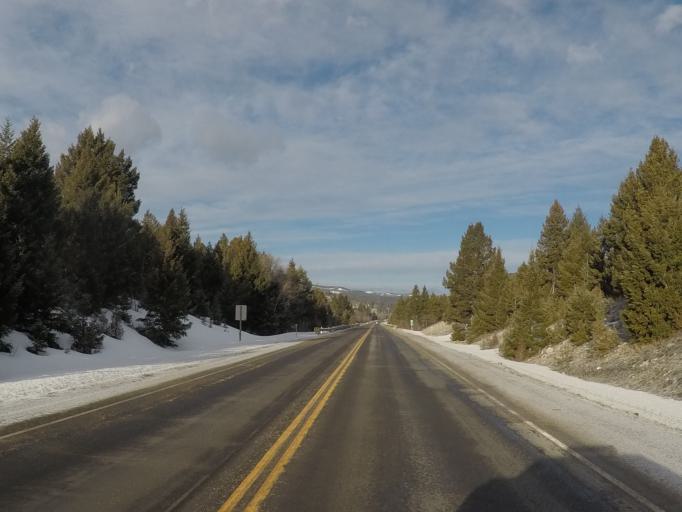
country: US
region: Montana
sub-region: Deer Lodge County
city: Anaconda
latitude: 46.1627
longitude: -113.0970
